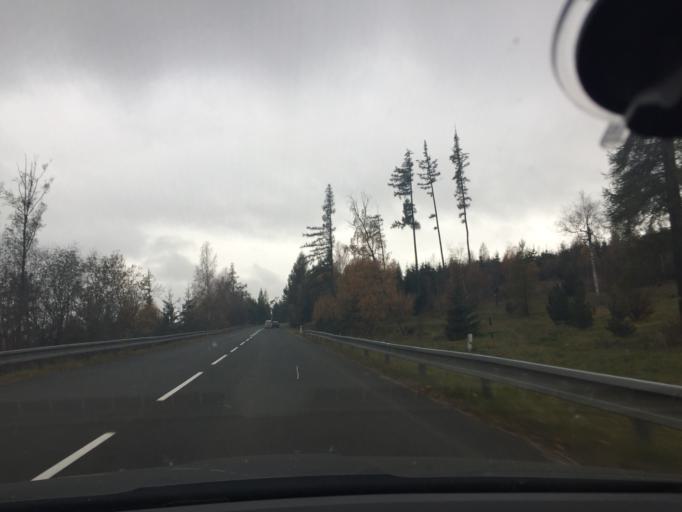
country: SK
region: Presovsky
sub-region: Okres Poprad
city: Svit
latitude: 49.1191
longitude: 20.1679
